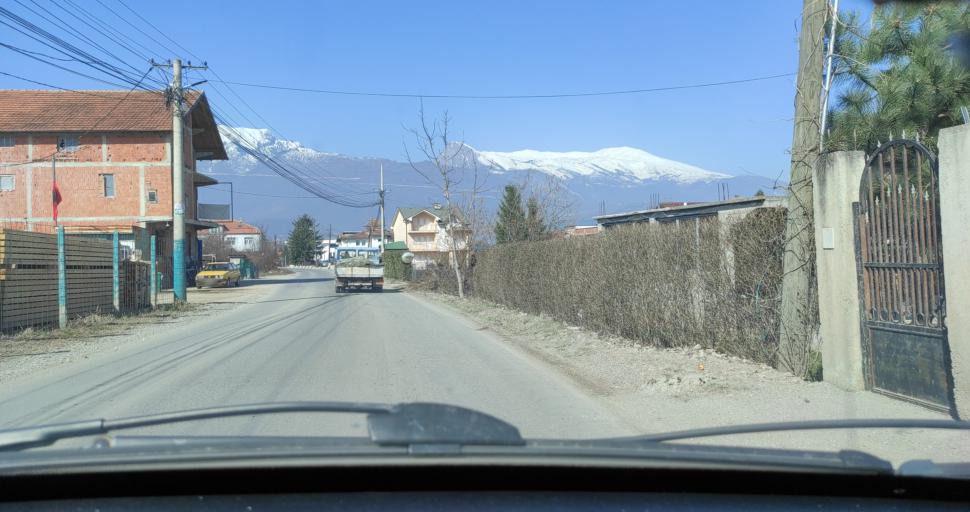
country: XK
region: Pec
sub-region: Komuna e Pejes
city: Peje
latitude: 42.6410
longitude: 20.3012
